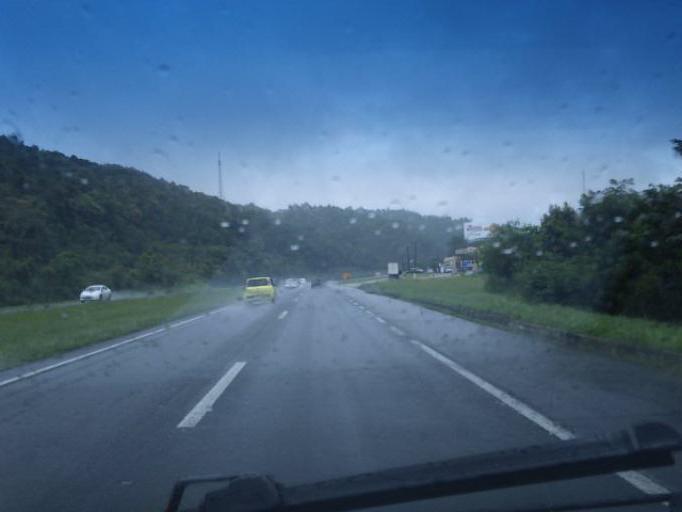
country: BR
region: Parana
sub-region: Campina Grande Do Sul
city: Campina Grande do Sul
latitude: -25.2563
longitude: -48.9129
